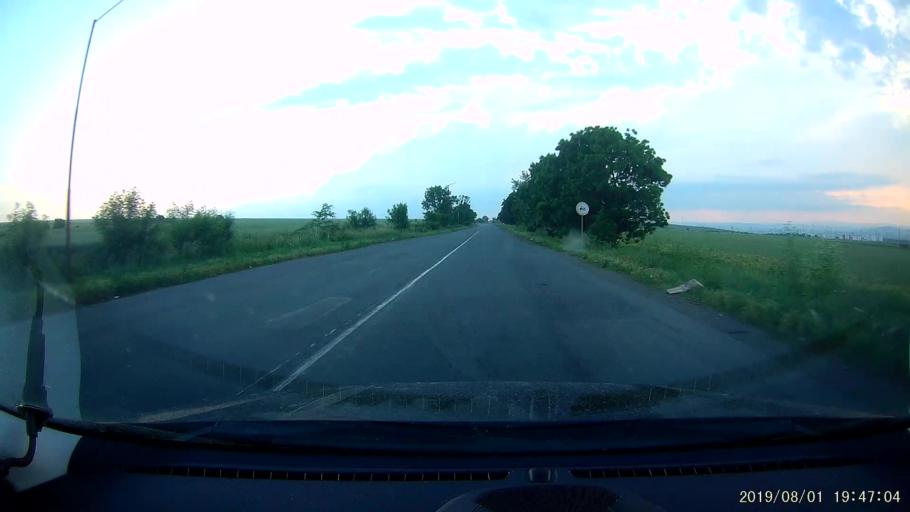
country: BG
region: Burgas
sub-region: Obshtina Karnobat
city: Karnobat
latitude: 42.6506
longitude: 26.9626
